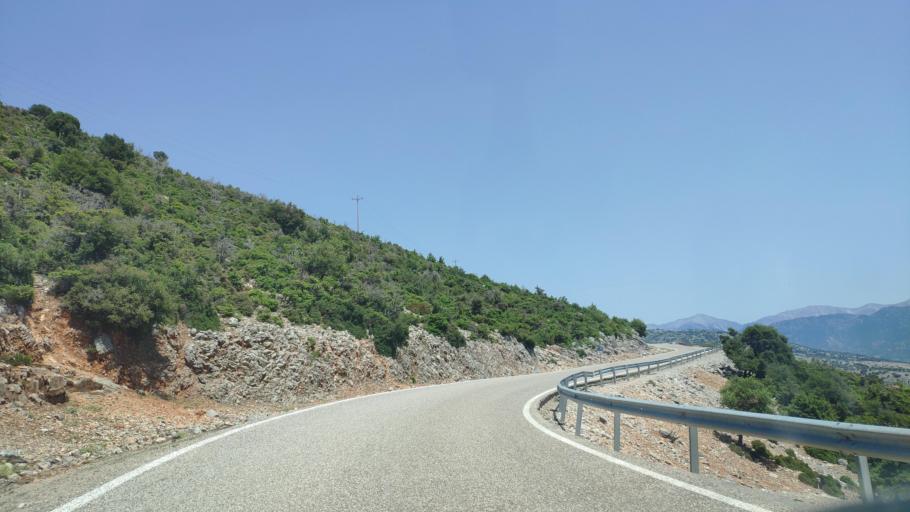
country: GR
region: West Greece
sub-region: Nomos Aitolias kai Akarnanias
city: Krikellos
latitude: 39.0512
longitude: 21.3828
